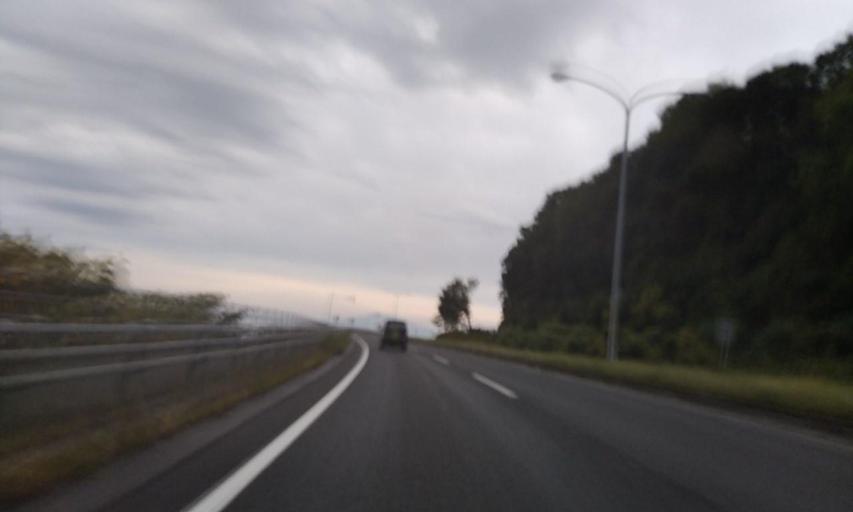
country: JP
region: Hokkaido
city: Abashiri
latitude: 44.0028
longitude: 144.2874
